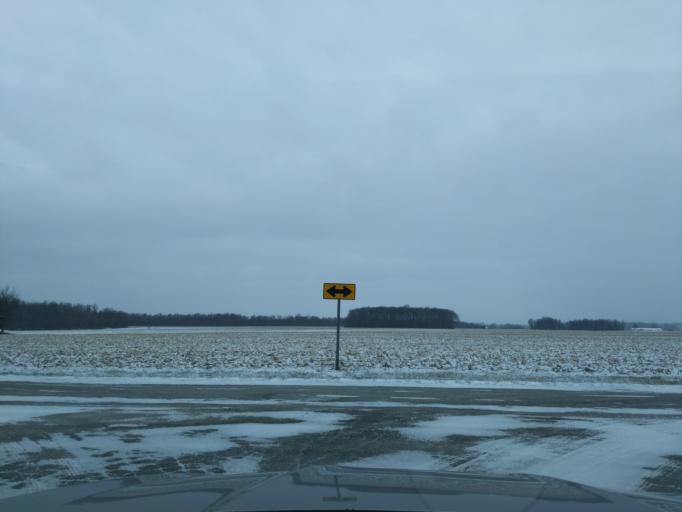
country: US
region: Indiana
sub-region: Decatur County
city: Greensburg
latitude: 39.2481
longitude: -85.4472
